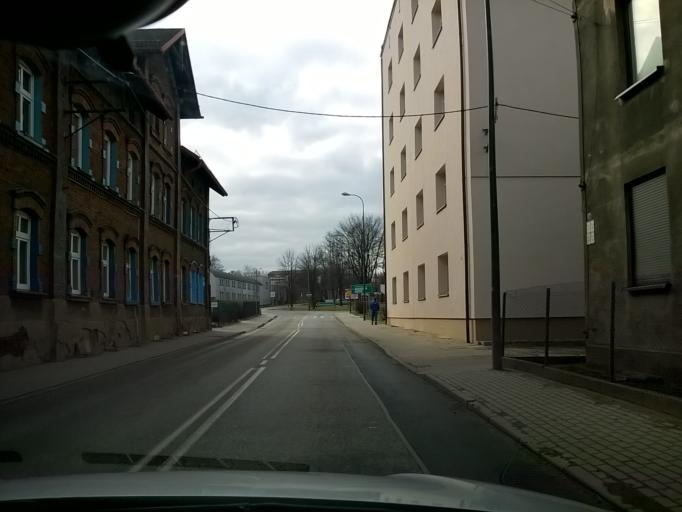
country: PL
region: Silesian Voivodeship
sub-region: Chorzow
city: Chorzow
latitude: 50.3233
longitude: 18.9759
